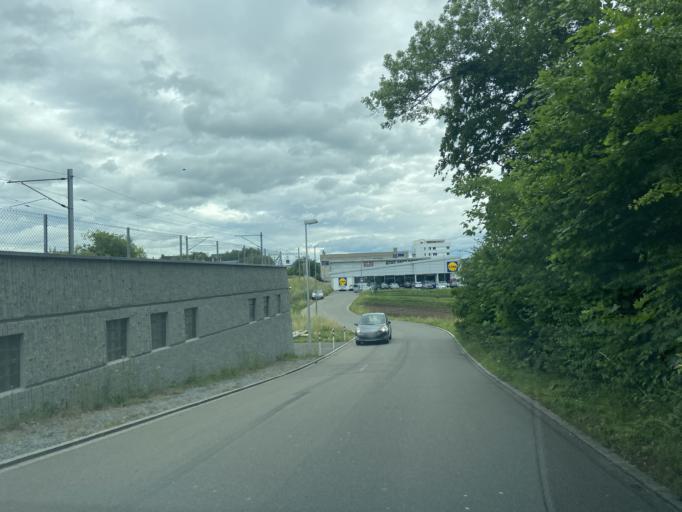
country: CH
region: Zurich
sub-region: Bezirk Buelach
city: Dietlikon / Dietlikon (Dorf)
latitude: 47.4117
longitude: 8.6119
